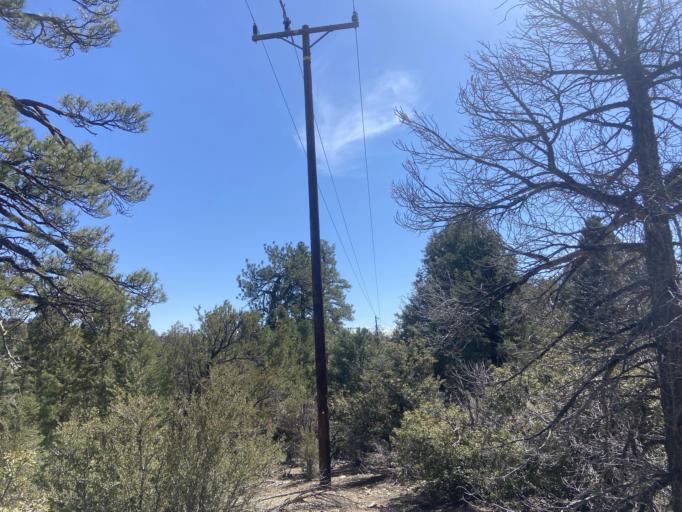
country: US
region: California
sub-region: San Bernardino County
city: Big Bear Lake
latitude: 34.3194
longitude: -116.9272
